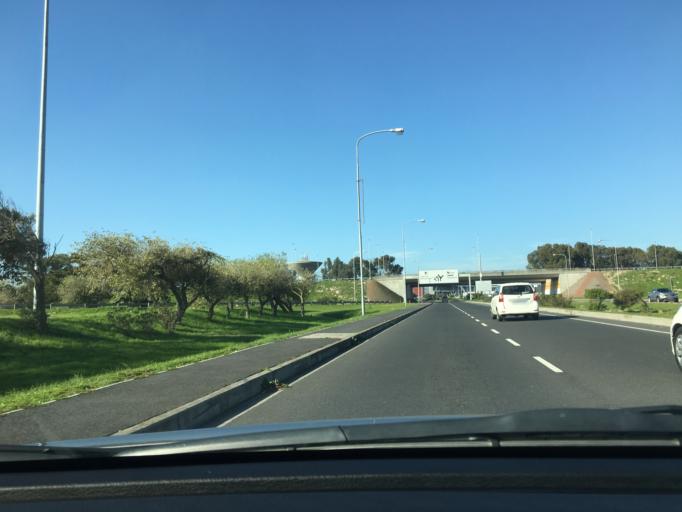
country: ZA
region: Western Cape
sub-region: City of Cape Town
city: Lansdowne
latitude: -33.9684
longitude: 18.5878
